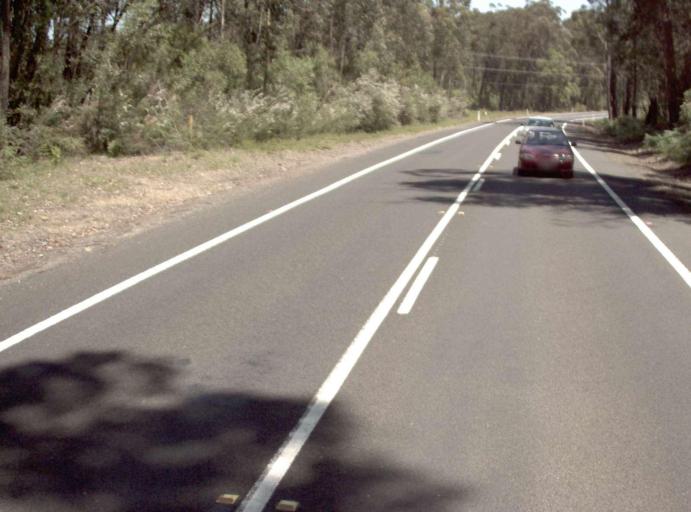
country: AU
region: Victoria
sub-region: East Gippsland
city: Lakes Entrance
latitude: -37.6987
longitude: 148.5877
